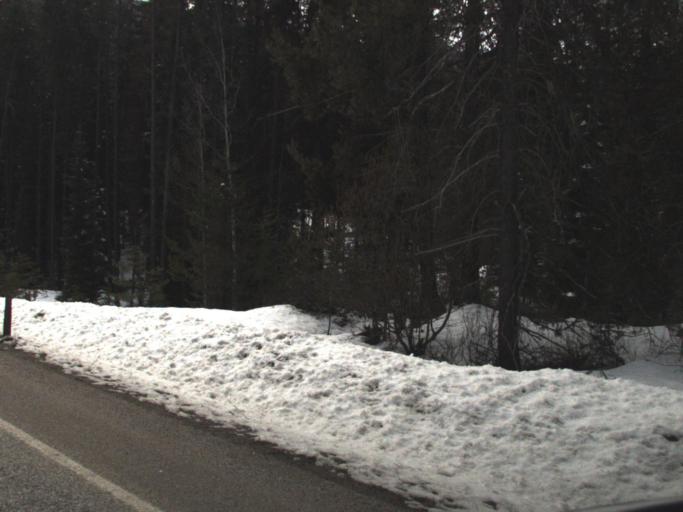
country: US
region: Washington
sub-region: Stevens County
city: Colville
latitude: 48.6527
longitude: -117.4934
